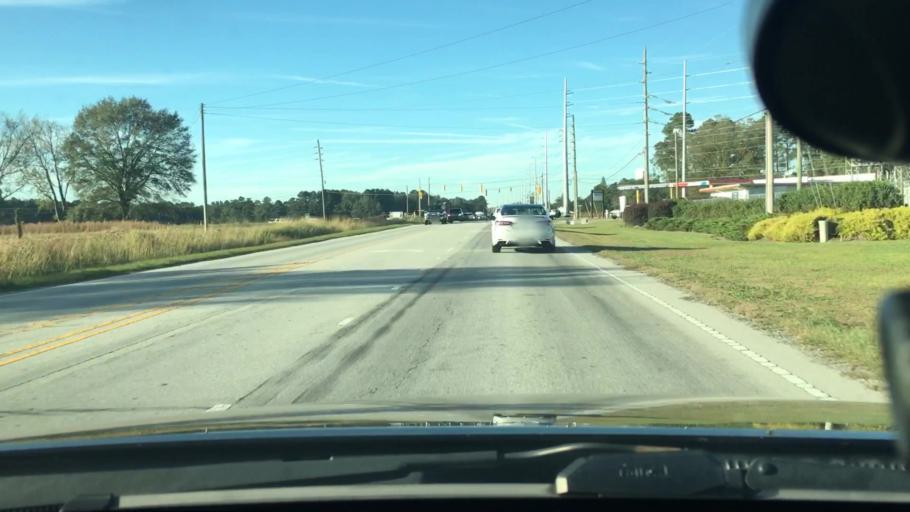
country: US
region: North Carolina
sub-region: Pitt County
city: Windsor
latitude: 35.5301
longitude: -77.3200
